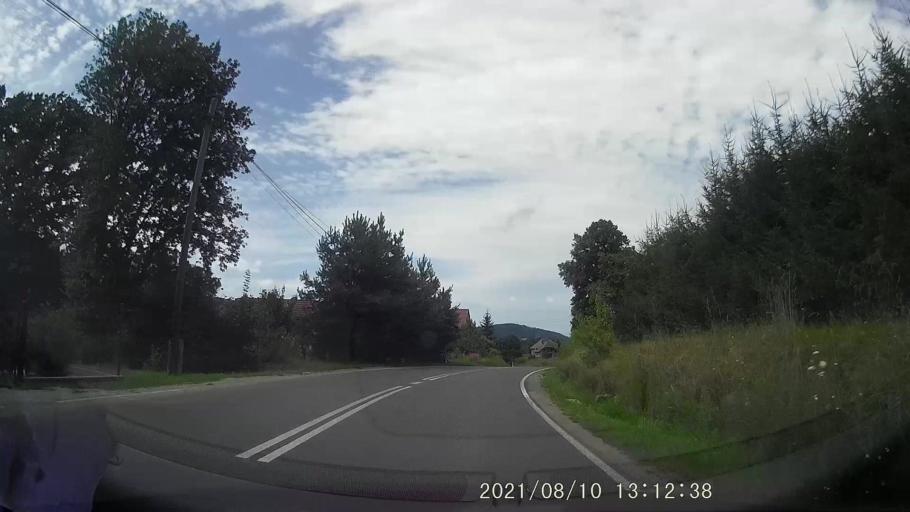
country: PL
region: Lower Silesian Voivodeship
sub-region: Powiat klodzki
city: Nowa Ruda
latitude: 50.5167
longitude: 16.5111
